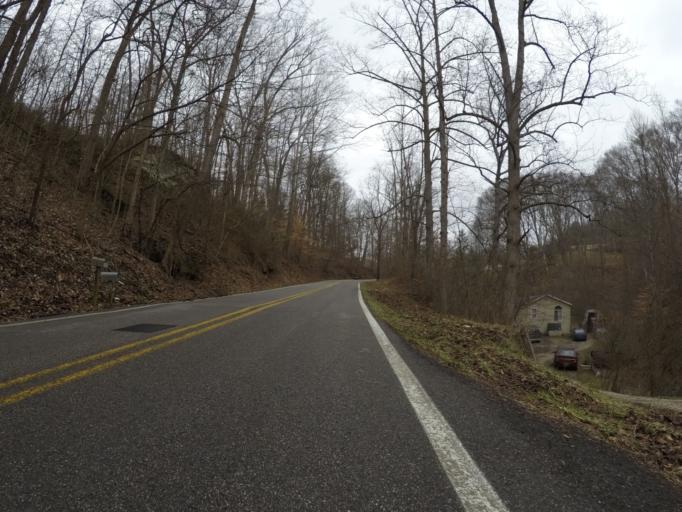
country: US
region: West Virginia
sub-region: Cabell County
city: Barboursville
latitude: 38.4544
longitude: -82.2646
